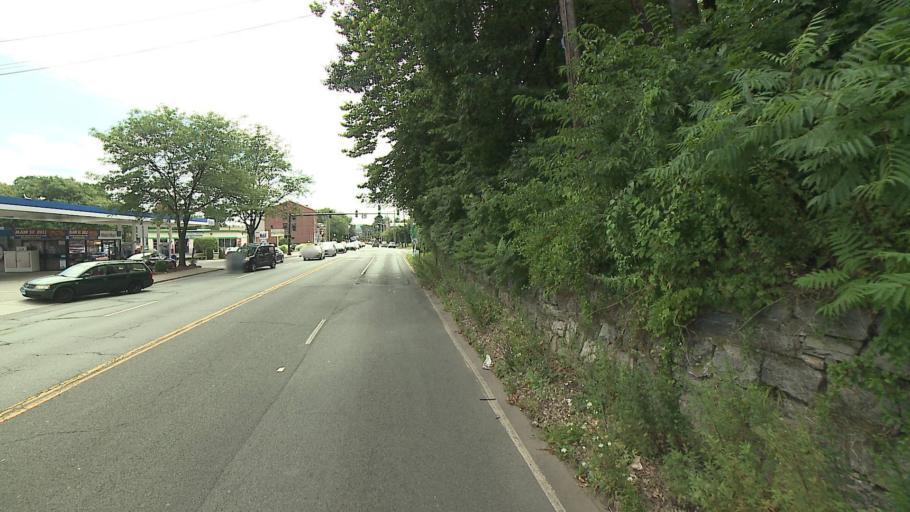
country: US
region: Connecticut
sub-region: Fairfield County
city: Danbury
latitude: 41.4043
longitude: -73.4596
